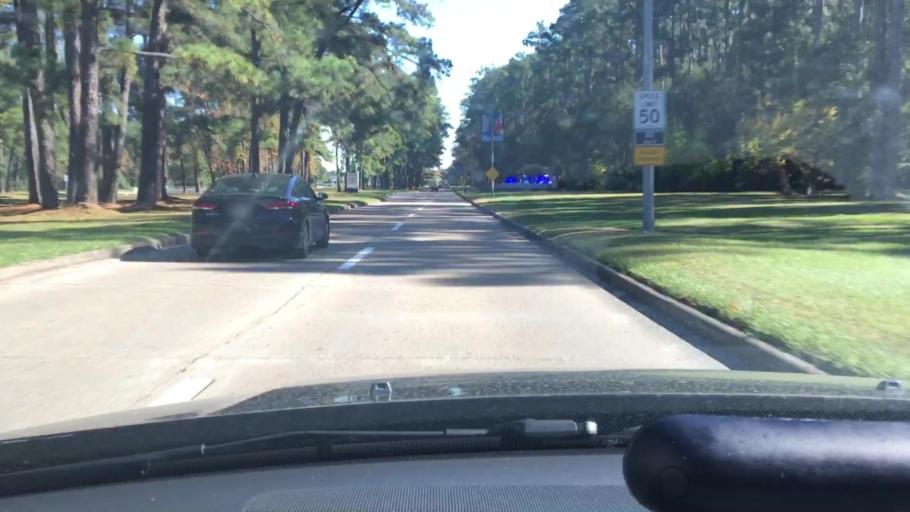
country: US
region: Texas
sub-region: Harris County
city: Humble
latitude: 29.9848
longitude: -95.3150
